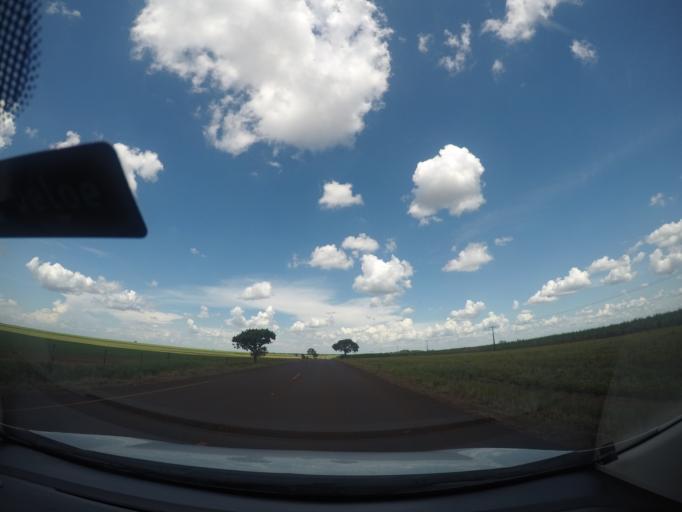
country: BR
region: Minas Gerais
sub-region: Frutal
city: Frutal
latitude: -19.9222
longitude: -48.6753
